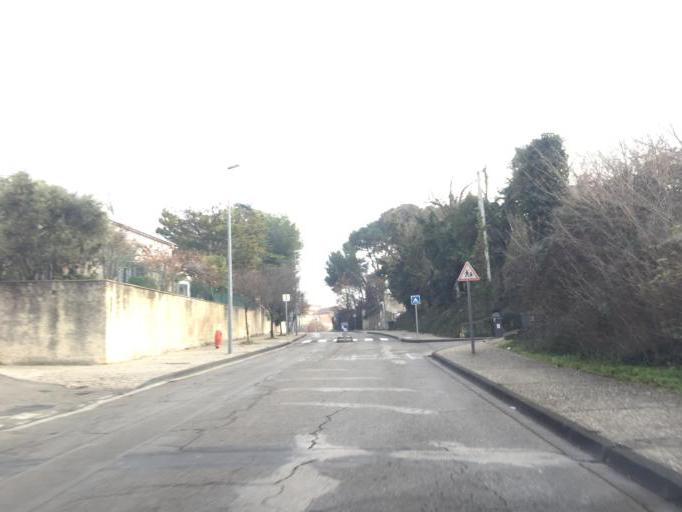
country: FR
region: Provence-Alpes-Cote d'Azur
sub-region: Departement du Vaucluse
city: Carpentras
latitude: 44.0549
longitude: 5.0384
